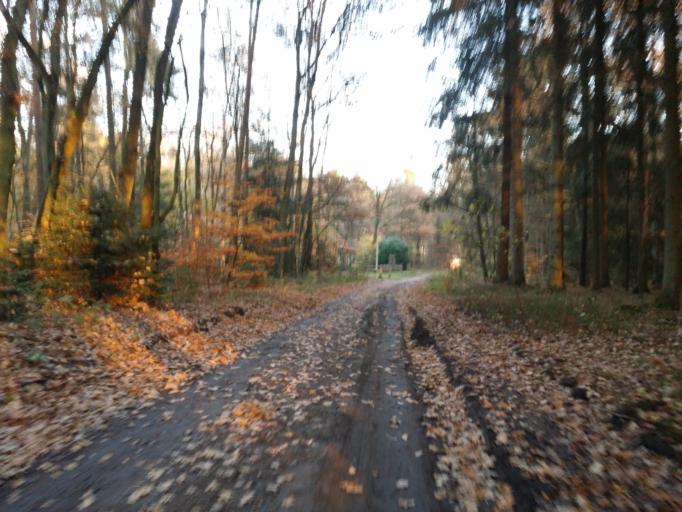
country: DE
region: Lower Saxony
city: Ahausen
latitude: 53.0755
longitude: 9.3018
